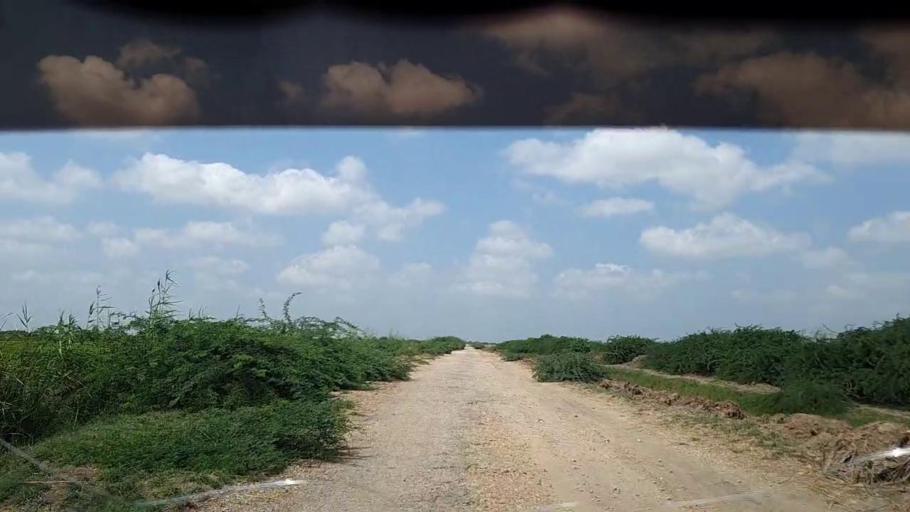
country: PK
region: Sindh
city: Kadhan
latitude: 24.5918
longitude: 68.9667
